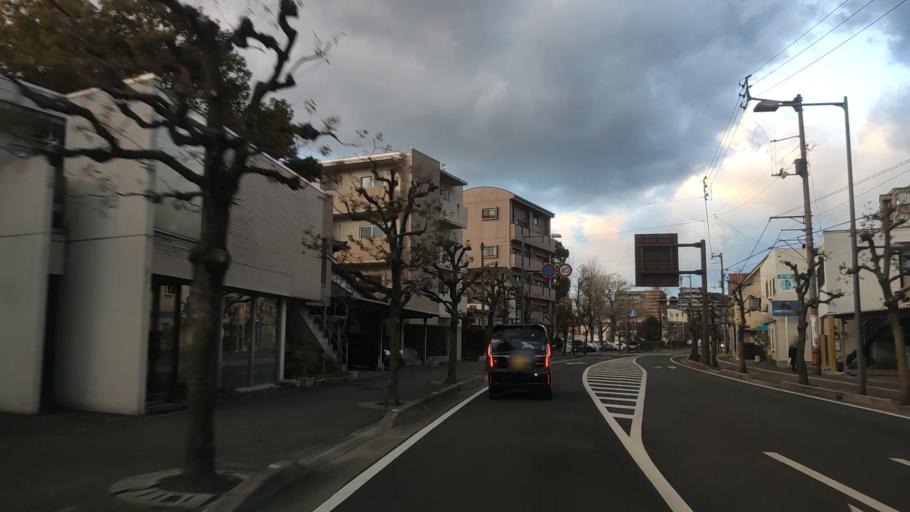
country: JP
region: Ehime
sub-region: Shikoku-chuo Shi
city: Matsuyama
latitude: 33.8417
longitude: 132.7846
